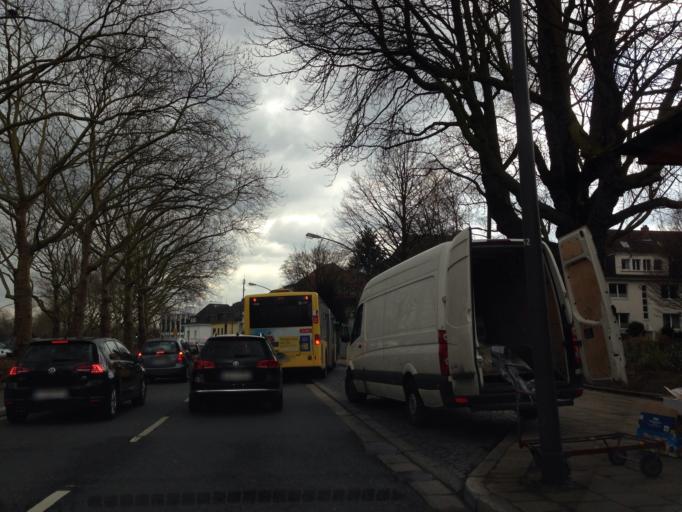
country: DE
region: North Rhine-Westphalia
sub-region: Regierungsbezirk Dusseldorf
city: Essen
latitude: 51.4440
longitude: 7.0318
